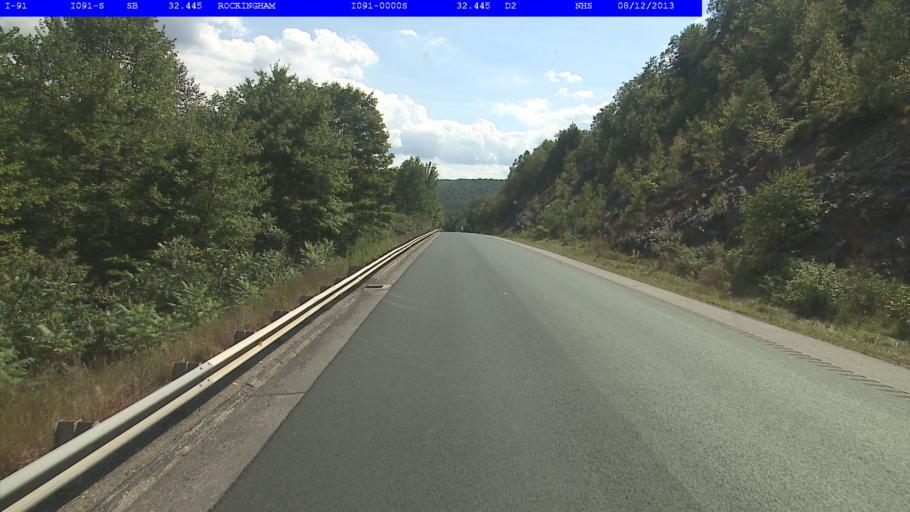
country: US
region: Vermont
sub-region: Windham County
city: Bellows Falls
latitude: 43.1417
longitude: -72.4758
